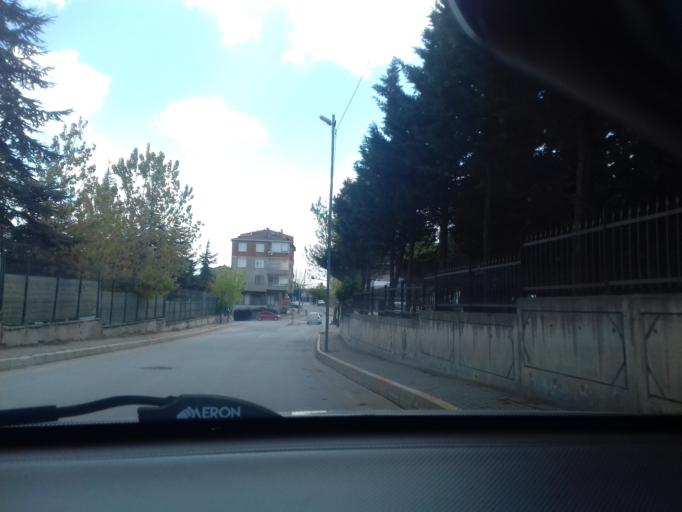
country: TR
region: Istanbul
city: Pendik
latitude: 40.8872
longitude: 29.2833
